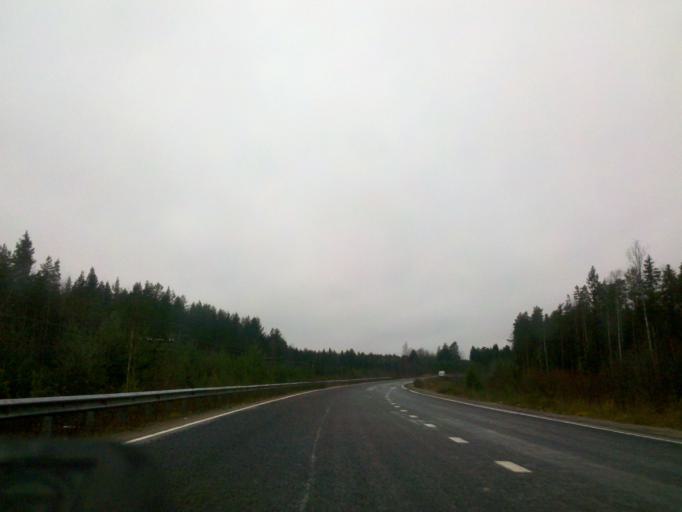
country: RU
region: Republic of Karelia
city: Shuya
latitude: 61.8510
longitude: 34.1948
